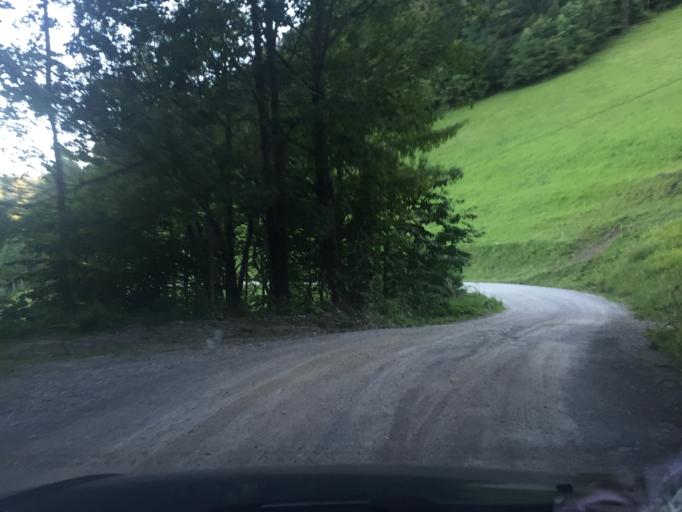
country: SI
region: Ravne na Koroskem
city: Kotlje
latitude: 46.4602
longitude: 14.9964
